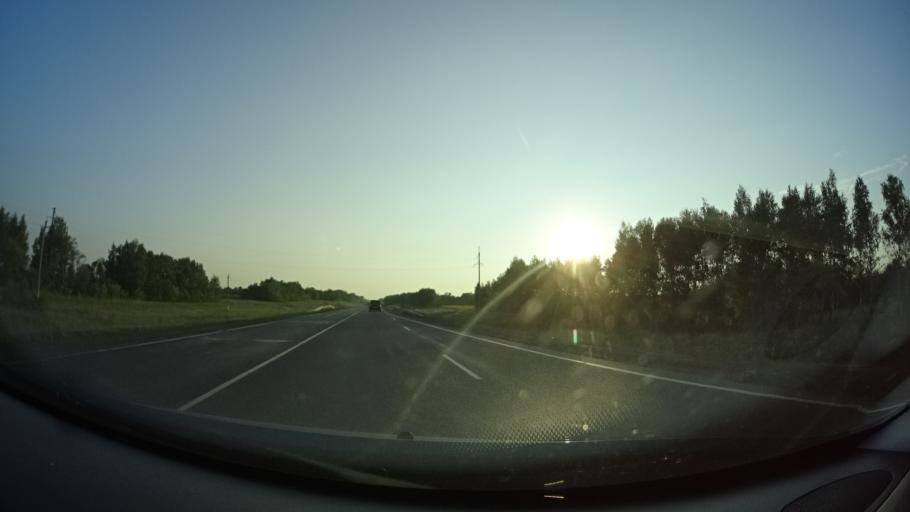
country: RU
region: Samara
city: Isakly
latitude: 54.0165
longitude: 51.7621
